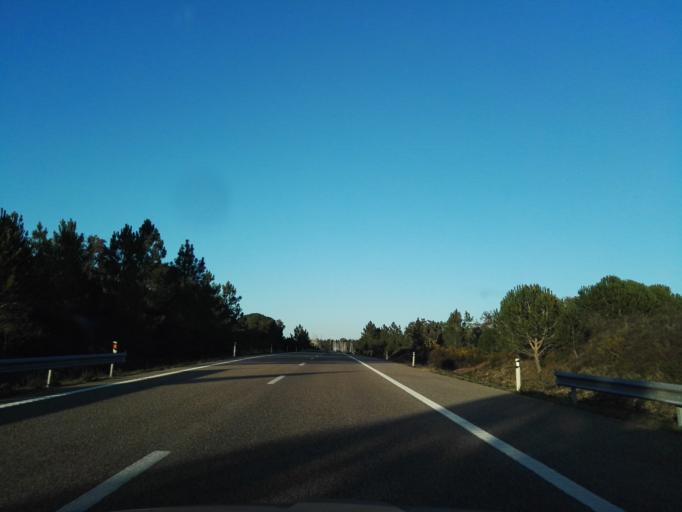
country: PT
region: Evora
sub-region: Vendas Novas
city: Vendas Novas
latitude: 38.6042
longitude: -8.6400
